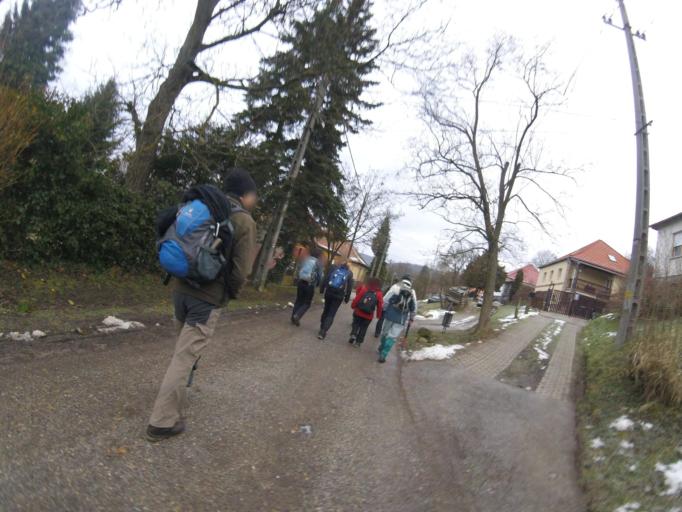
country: HU
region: Pest
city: Visegrad
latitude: 47.7261
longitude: 18.9904
